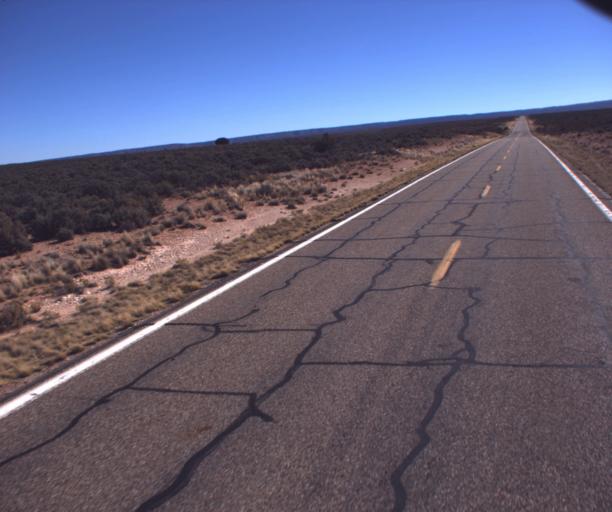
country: US
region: Arizona
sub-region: Coconino County
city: Fredonia
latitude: 36.9025
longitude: -112.3810
